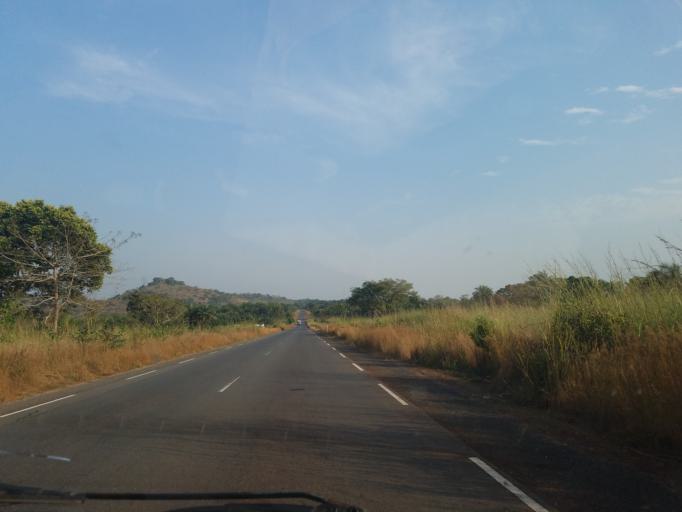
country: GN
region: Boke
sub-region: Boffa
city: Boffa
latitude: 10.3492
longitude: -14.2487
